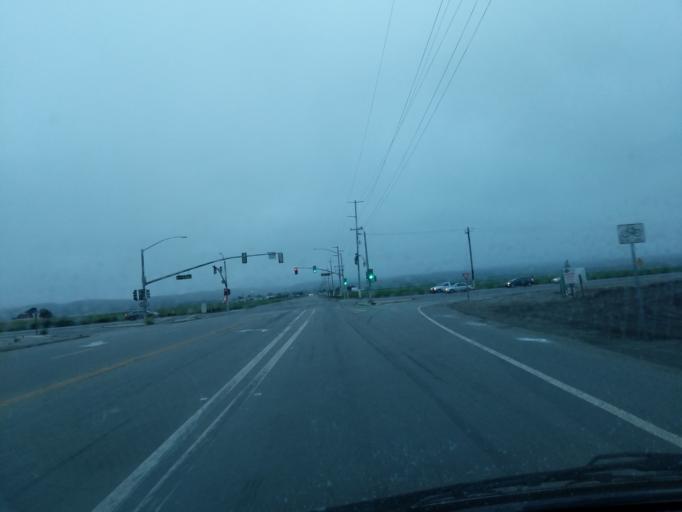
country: US
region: California
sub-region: Monterey County
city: Salinas
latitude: 36.6675
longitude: -121.6846
